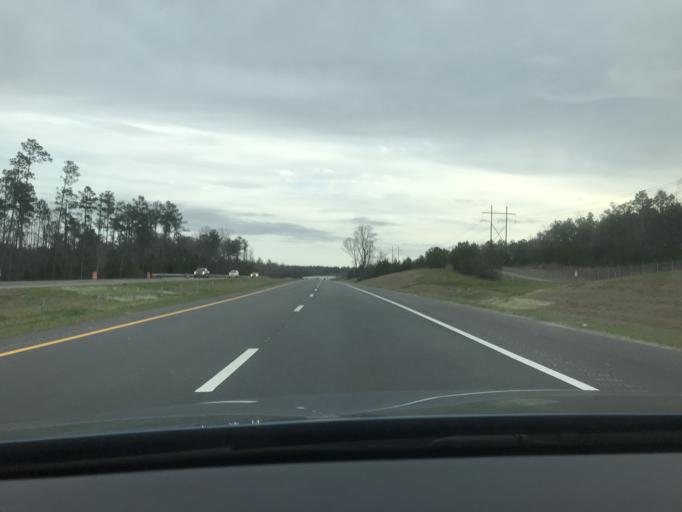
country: US
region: North Carolina
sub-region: Cumberland County
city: Fort Bragg
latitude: 35.0883
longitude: -79.0255
